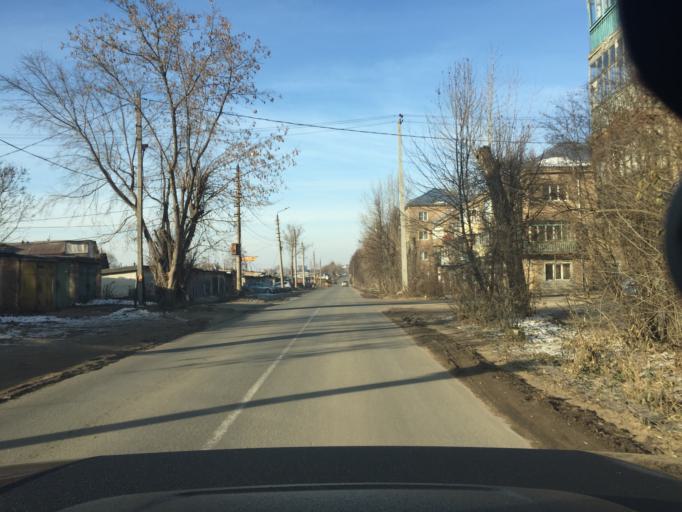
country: RU
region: Tula
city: Tula
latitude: 54.1798
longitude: 37.7005
